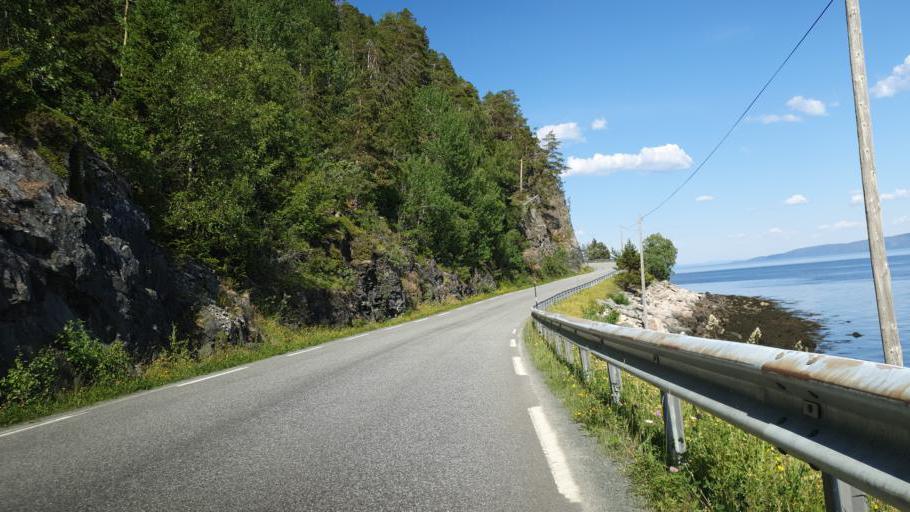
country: NO
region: Nord-Trondelag
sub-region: Leksvik
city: Leksvik
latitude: 63.6452
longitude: 10.5993
